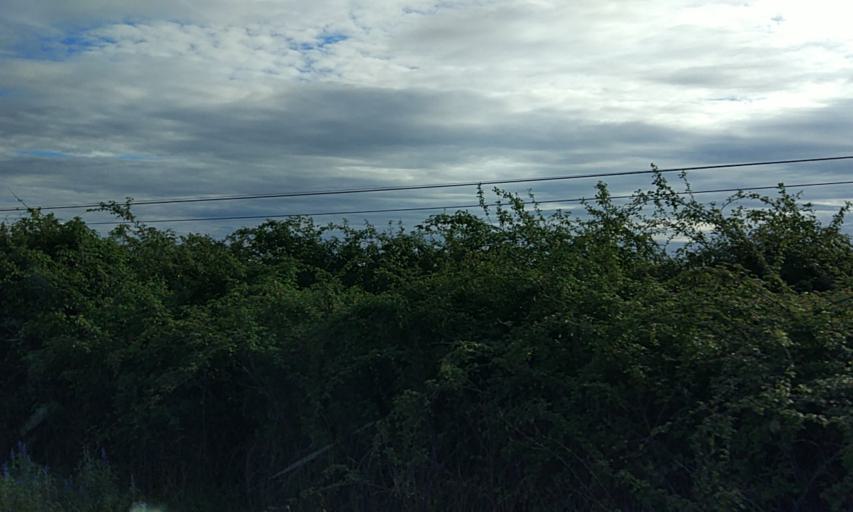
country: ES
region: Extremadura
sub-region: Provincia de Caceres
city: Moraleja
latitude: 40.0535
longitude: -6.6422
